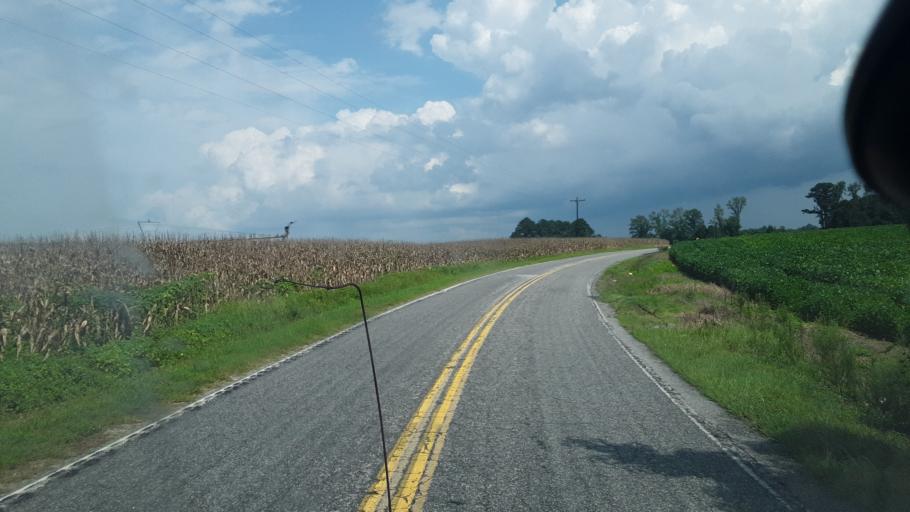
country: US
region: South Carolina
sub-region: Lee County
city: Bishopville
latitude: 34.1783
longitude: -80.1491
